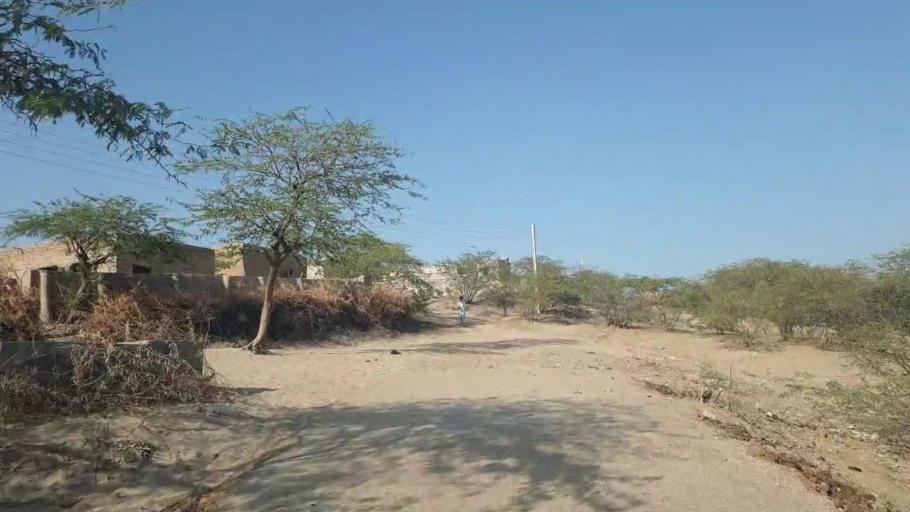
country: PK
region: Sindh
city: Chor
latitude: 25.5376
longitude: 69.6971
